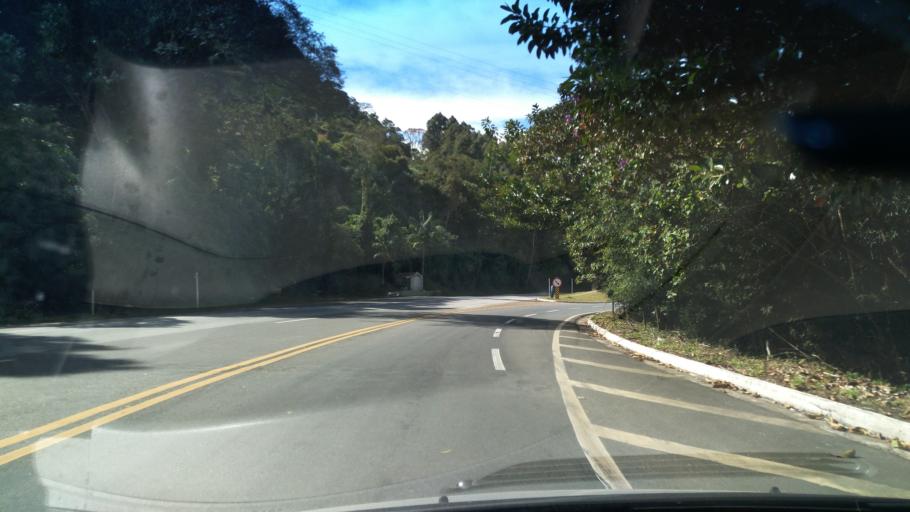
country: BR
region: Minas Gerais
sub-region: Borda Da Mata
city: Borda da Mata
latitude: -22.1308
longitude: -46.1800
